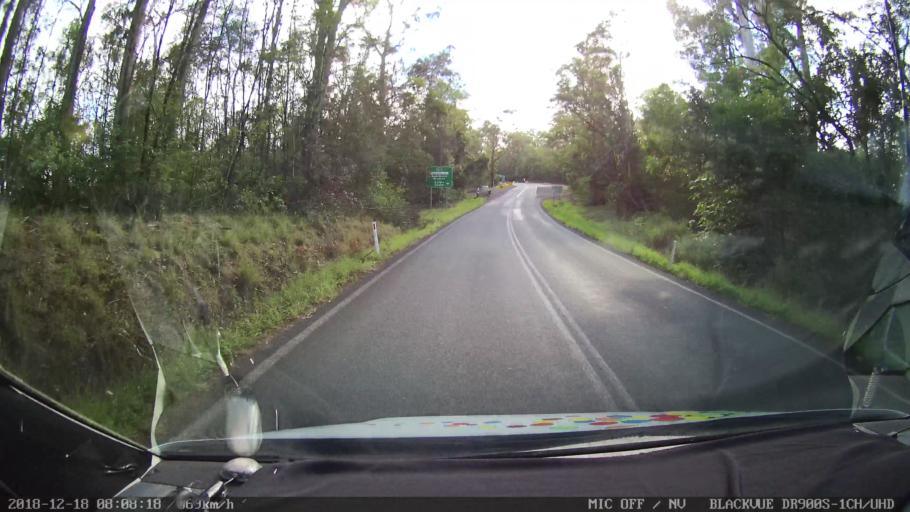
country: AU
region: New South Wales
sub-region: Kyogle
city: Kyogle
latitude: -28.3819
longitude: 152.6505
